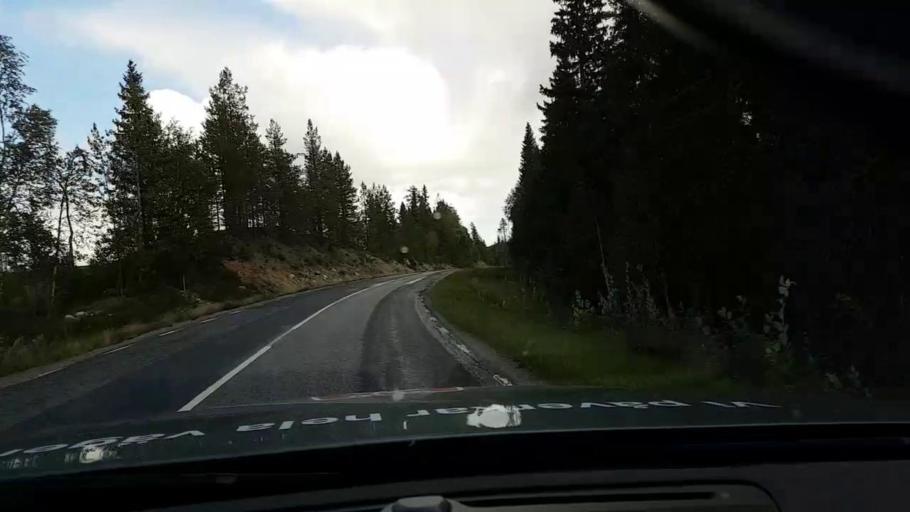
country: SE
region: Vaesterbotten
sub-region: Asele Kommun
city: Asele
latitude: 63.8338
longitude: 17.4474
